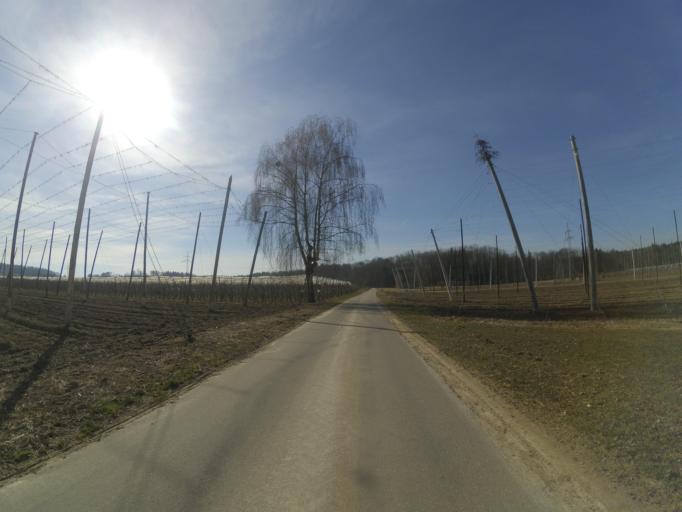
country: DE
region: Baden-Wuerttemberg
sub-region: Tuebingen Region
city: Meckenbeuren
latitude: 47.7215
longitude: 9.5802
